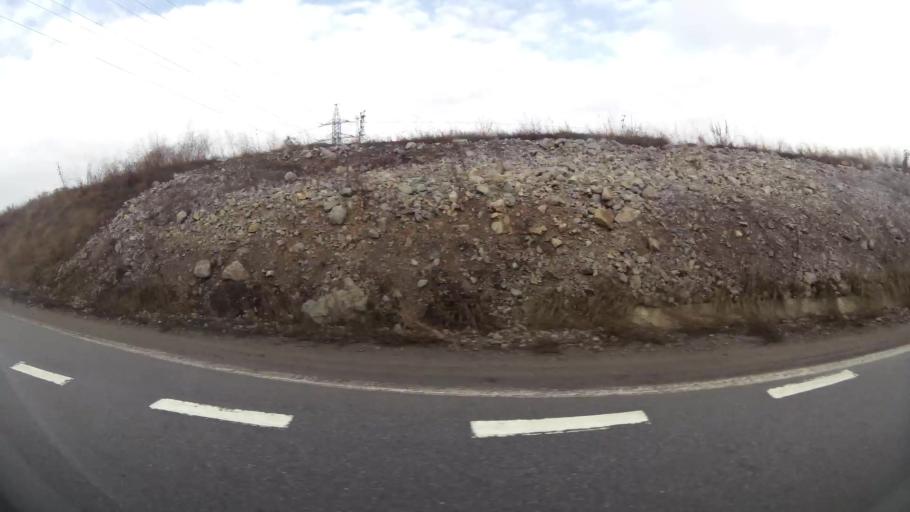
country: BG
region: Sofiya
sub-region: Obshtina Bozhurishte
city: Bozhurishte
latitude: 42.7139
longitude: 23.2294
